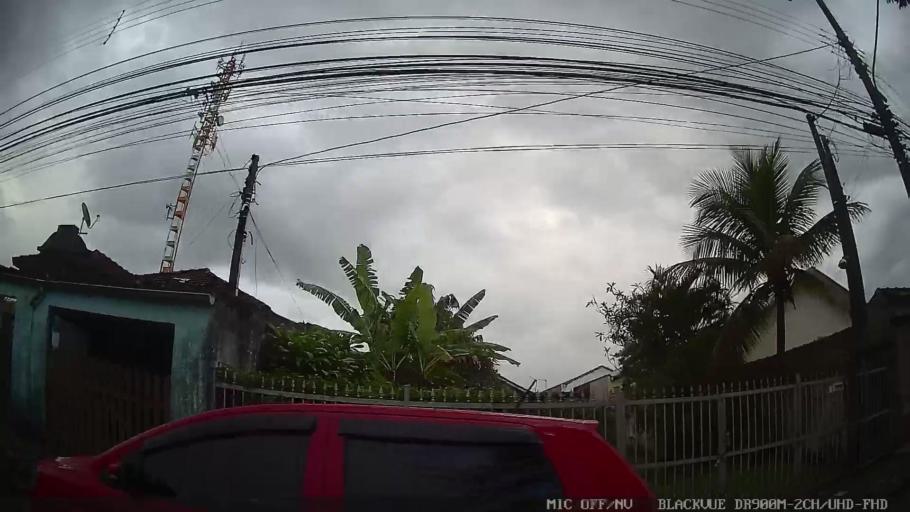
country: BR
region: Sao Paulo
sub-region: Itanhaem
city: Itanhaem
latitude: -24.1812
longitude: -46.7865
